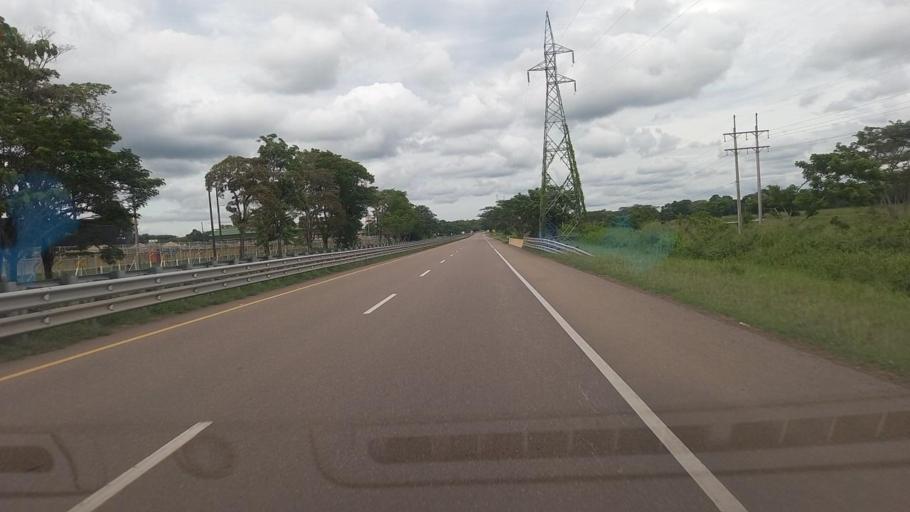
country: CO
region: Boyaca
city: Puerto Boyaca
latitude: 6.0626
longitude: -74.5585
